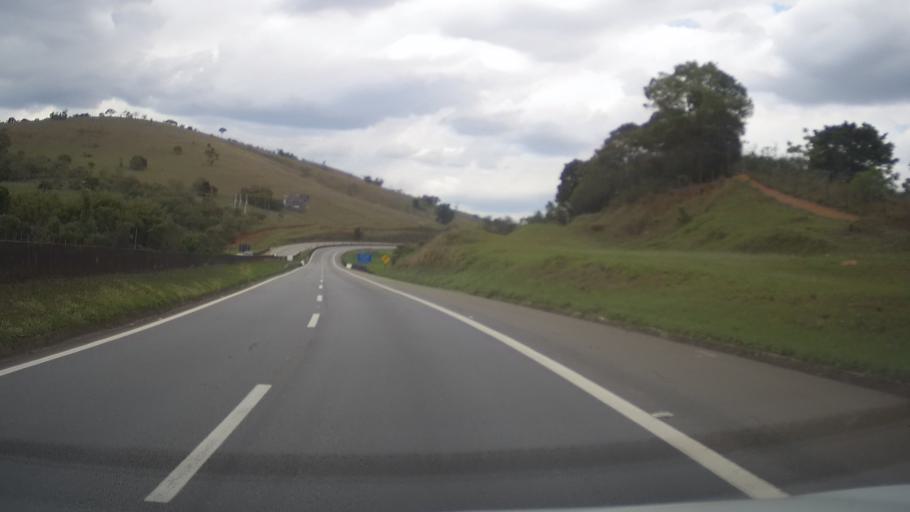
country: BR
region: Minas Gerais
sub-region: Tres Coracoes
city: Tres Coracoes
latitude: -21.5220
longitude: -45.2237
